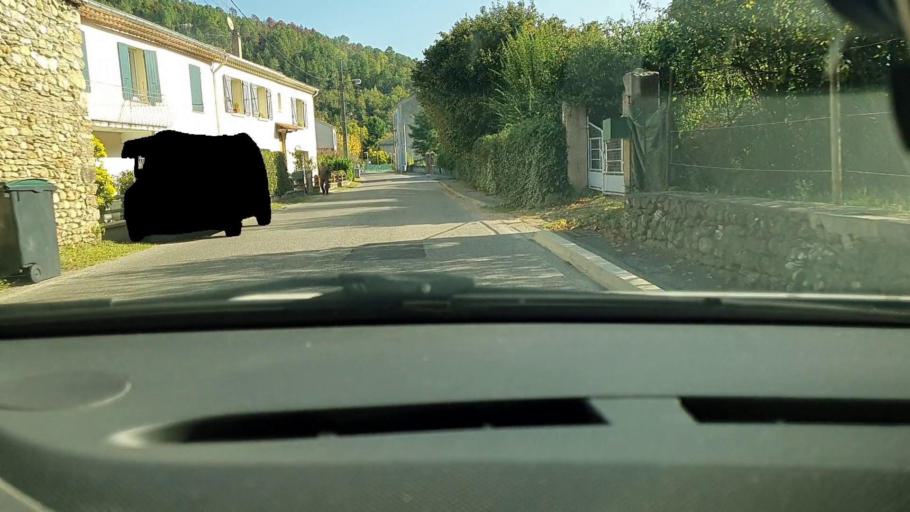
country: FR
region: Languedoc-Roussillon
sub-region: Departement du Gard
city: Besseges
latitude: 44.2994
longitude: 4.0817
